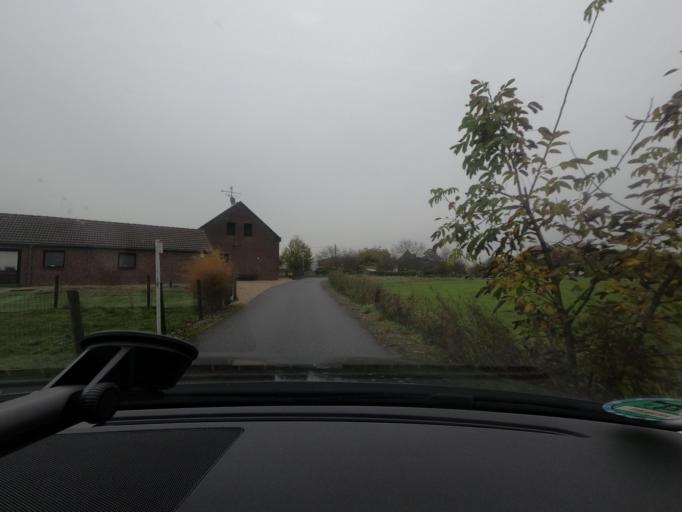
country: DE
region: North Rhine-Westphalia
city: Kempen
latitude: 51.3816
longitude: 6.3845
